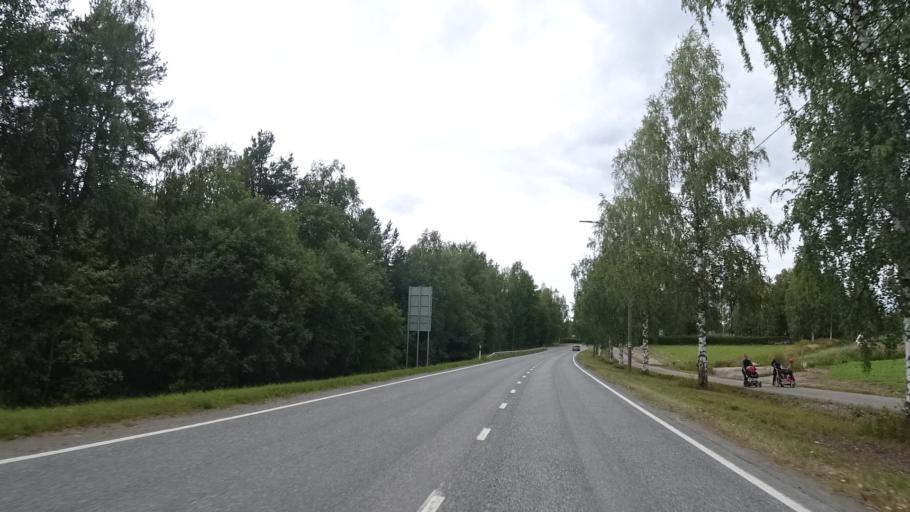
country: FI
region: North Karelia
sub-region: Joensuu
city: Ilomantsi
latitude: 62.6561
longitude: 30.9341
